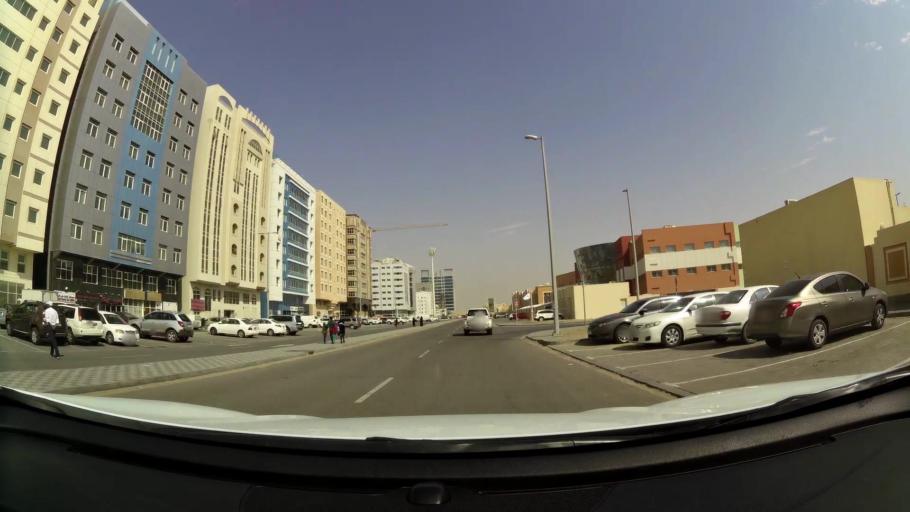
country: AE
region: Abu Dhabi
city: Abu Dhabi
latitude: 24.3399
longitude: 54.5314
